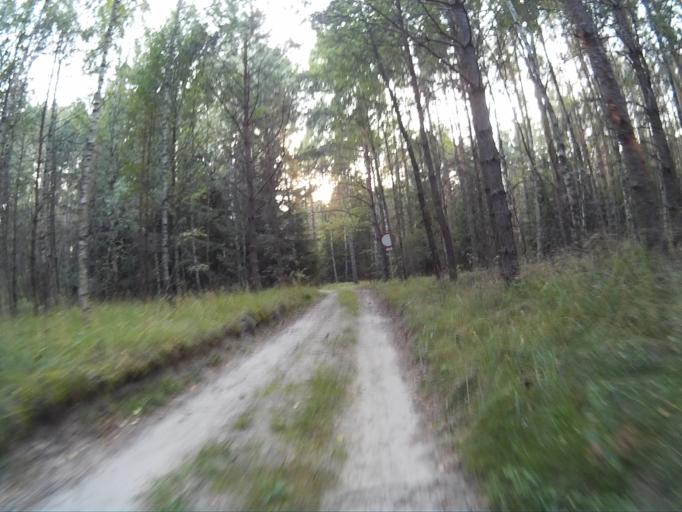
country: PL
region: Pomeranian Voivodeship
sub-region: Powiat chojnicki
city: Czersk
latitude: 53.7218
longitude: 17.8997
